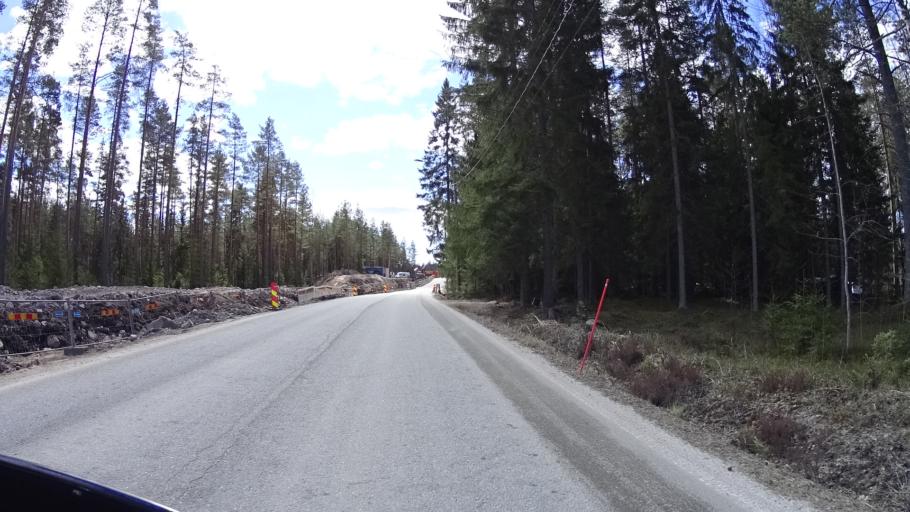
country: FI
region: Uusimaa
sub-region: Helsinki
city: Espoo
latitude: 60.2611
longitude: 24.5228
